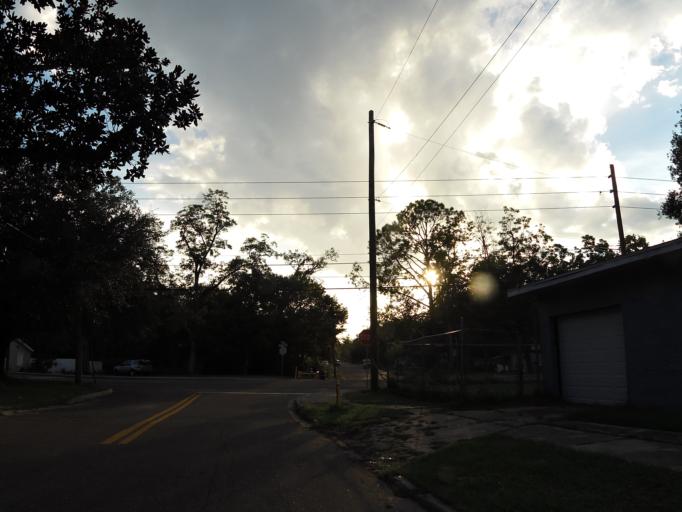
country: US
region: Florida
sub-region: Duval County
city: Jacksonville
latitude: 30.3347
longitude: -81.7052
